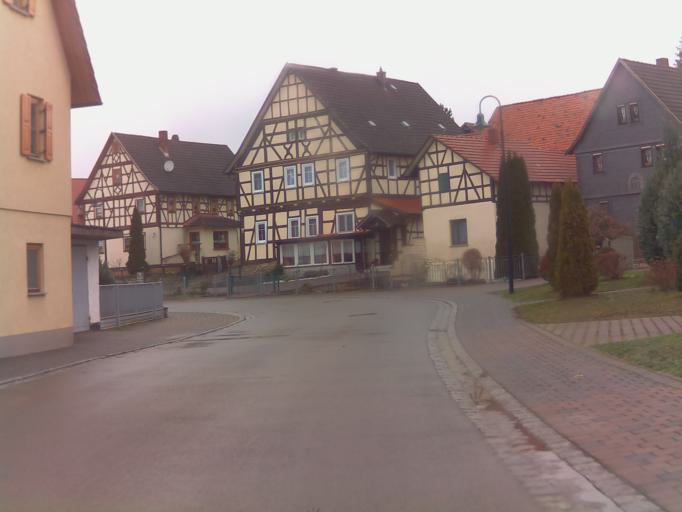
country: DE
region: Thuringia
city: Romhild
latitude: 50.4169
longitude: 10.5432
